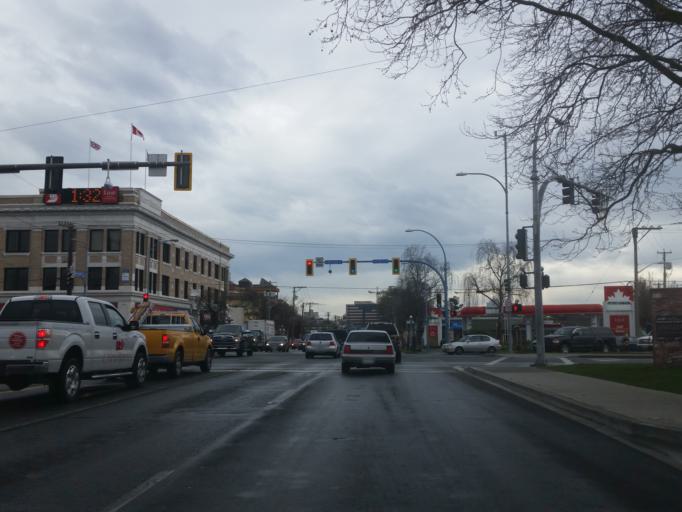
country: CA
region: British Columbia
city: Victoria
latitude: 48.4386
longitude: -123.3672
